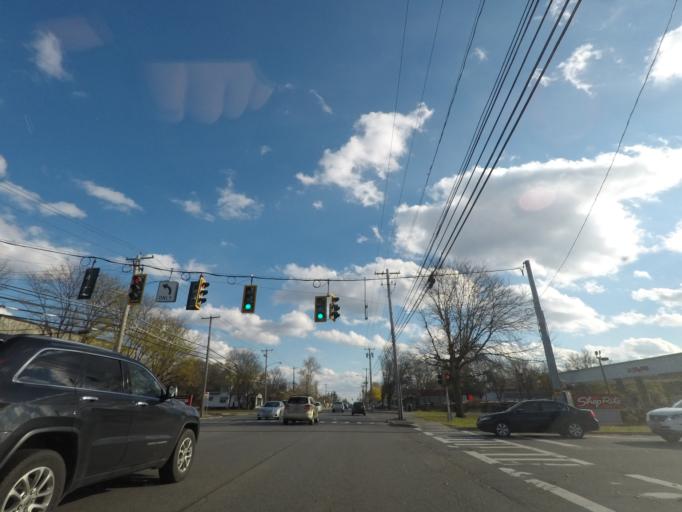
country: US
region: New York
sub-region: Albany County
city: Colonie
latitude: 42.7260
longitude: -73.8425
